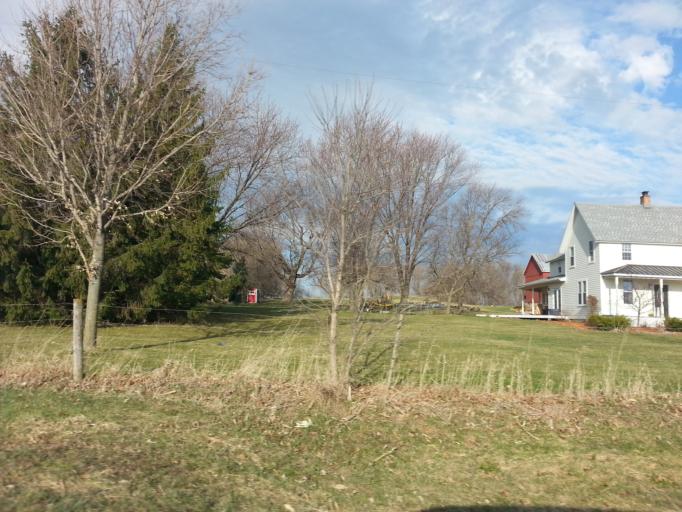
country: US
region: Minnesota
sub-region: Dakota County
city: Hastings
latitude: 44.8239
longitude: -92.8416
